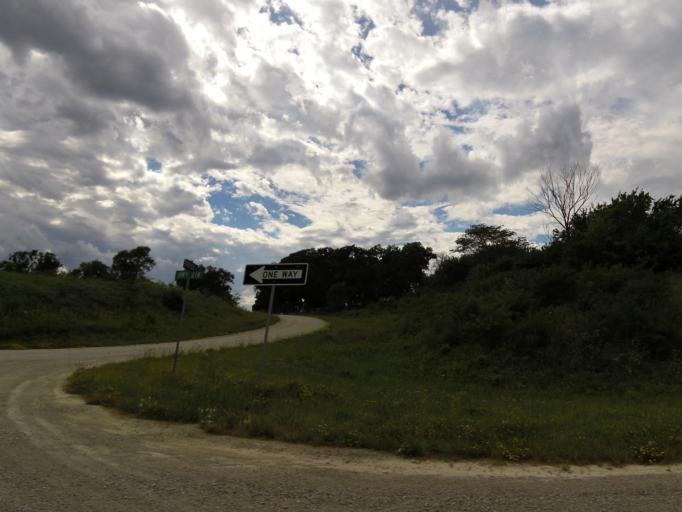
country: US
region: Iowa
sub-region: Henry County
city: Mount Pleasant
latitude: 40.9121
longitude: -91.5471
